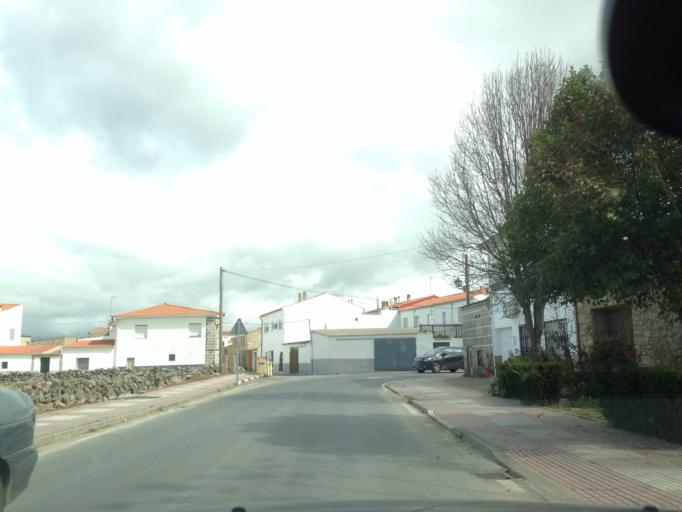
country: ES
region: Extremadura
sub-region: Provincia de Caceres
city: Albala
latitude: 39.2591
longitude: -6.1875
